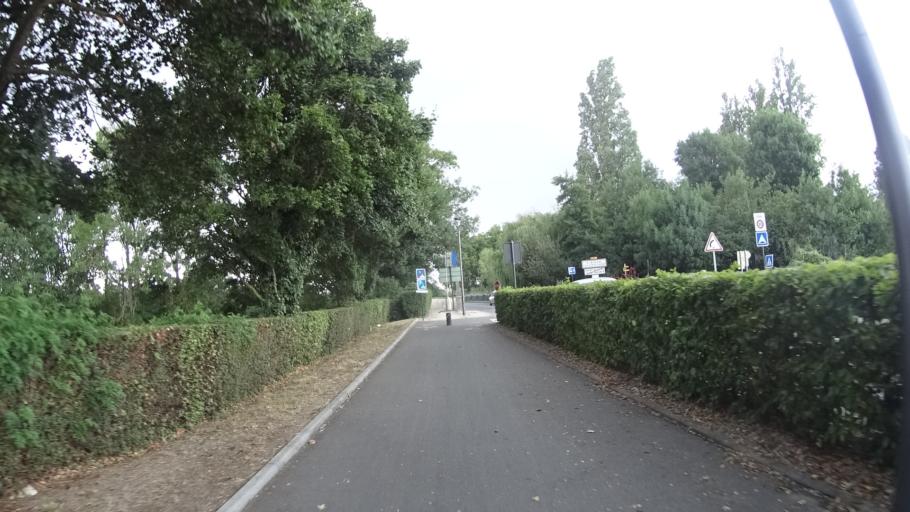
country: FR
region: Centre
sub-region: Departement du Loiret
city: Saint-Hilaire-Saint-Mesmin
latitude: 47.8716
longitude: 1.8398
